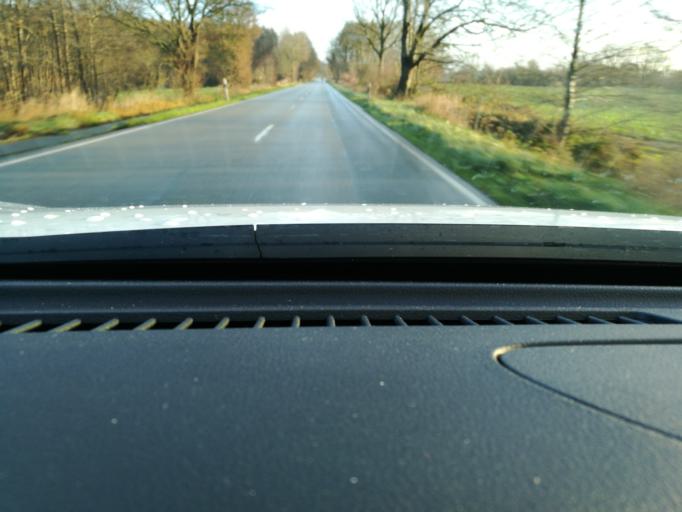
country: DE
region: Schleswig-Holstein
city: Holzbunge
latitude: 54.4077
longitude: 9.6834
